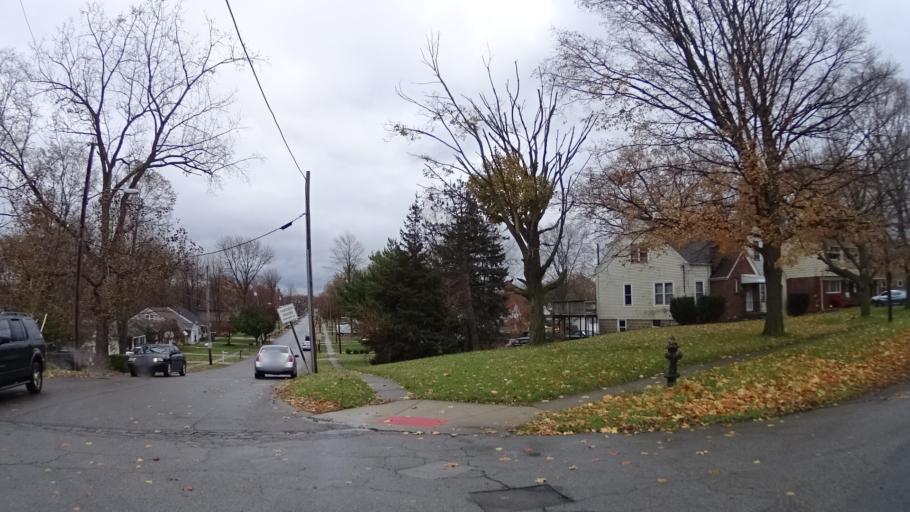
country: US
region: Ohio
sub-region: Lorain County
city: Elyria
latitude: 41.3874
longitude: -82.1293
